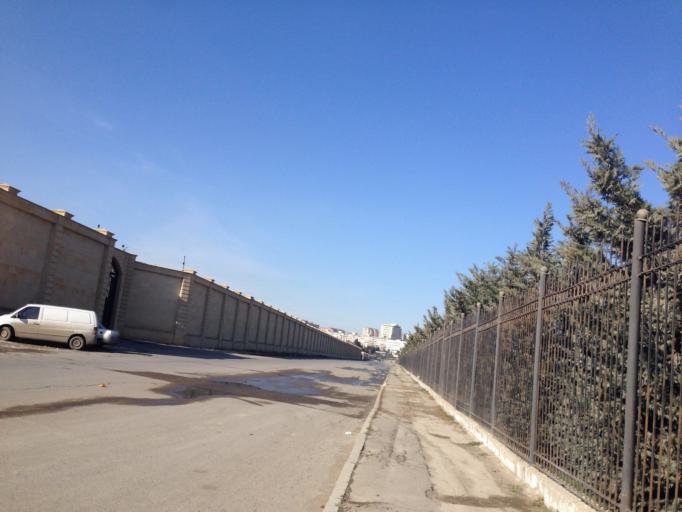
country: AZ
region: Baki
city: Baku
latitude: 40.4070
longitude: 49.8589
